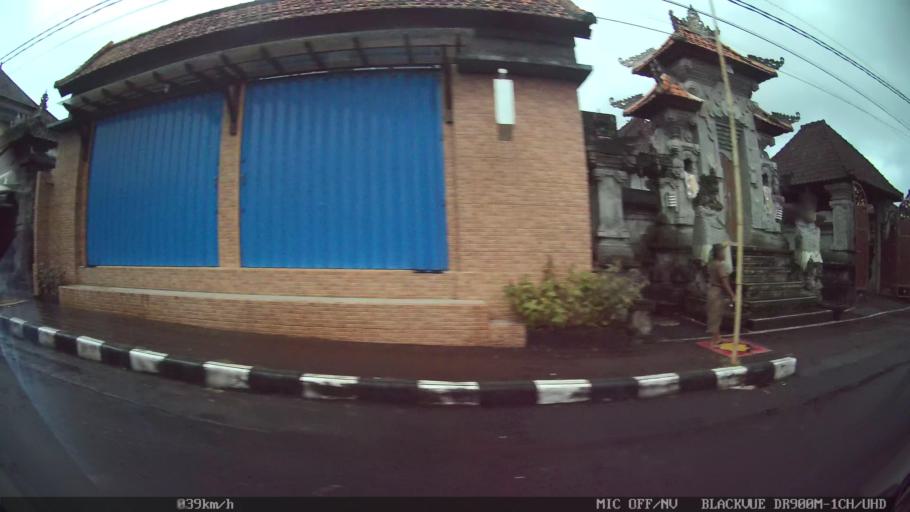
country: ID
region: Bali
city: Pegongan
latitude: -8.4903
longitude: 115.2263
